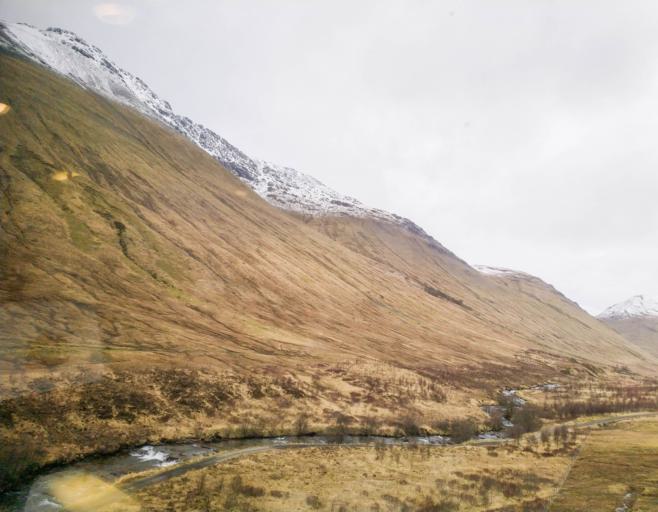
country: GB
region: Scotland
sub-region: Argyll and Bute
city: Garelochhead
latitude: 56.4889
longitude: -4.7046
